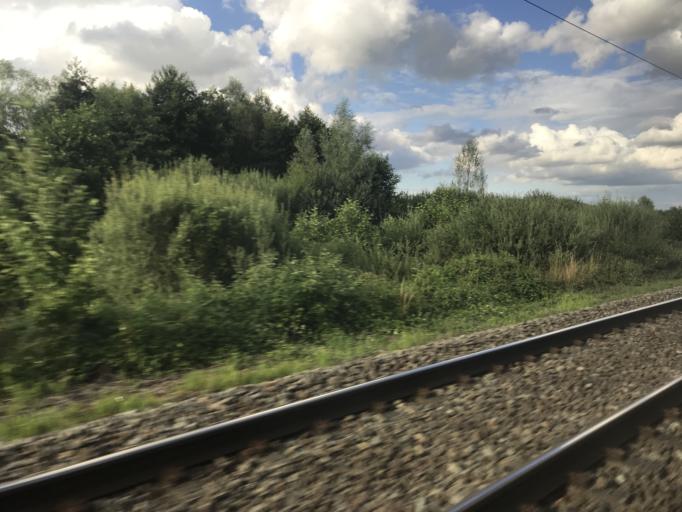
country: FR
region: Champagne-Ardenne
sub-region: Departement des Ardennes
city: Bazeilles
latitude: 49.6728
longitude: 5.0094
